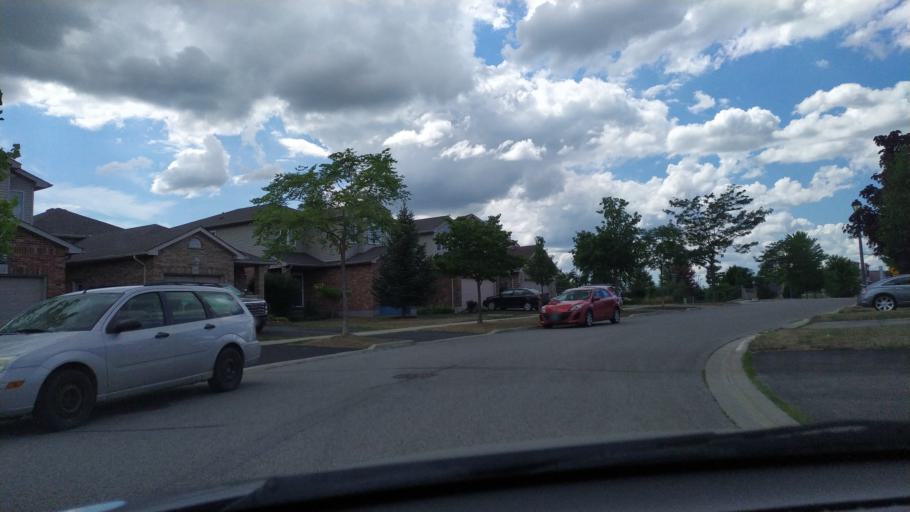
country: CA
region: Ontario
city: Stratford
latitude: 43.3775
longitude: -81.0014
